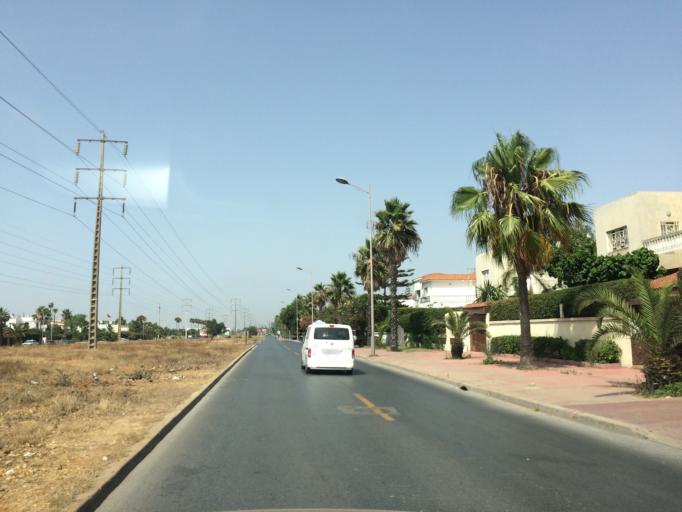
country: MA
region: Rabat-Sale-Zemmour-Zaer
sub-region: Skhirate-Temara
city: Temara
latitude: 33.9617
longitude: -6.8737
